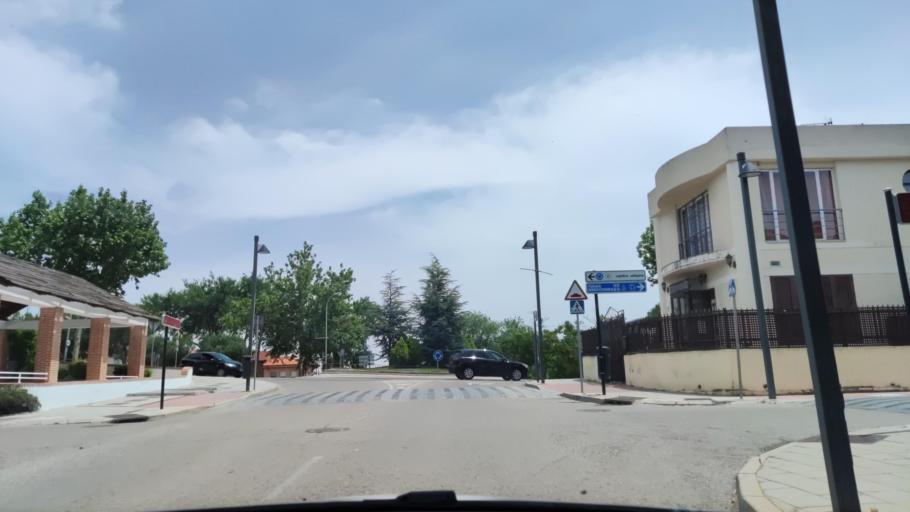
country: ES
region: Madrid
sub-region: Provincia de Madrid
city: Navalcarnero
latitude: 40.2857
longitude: -4.0218
